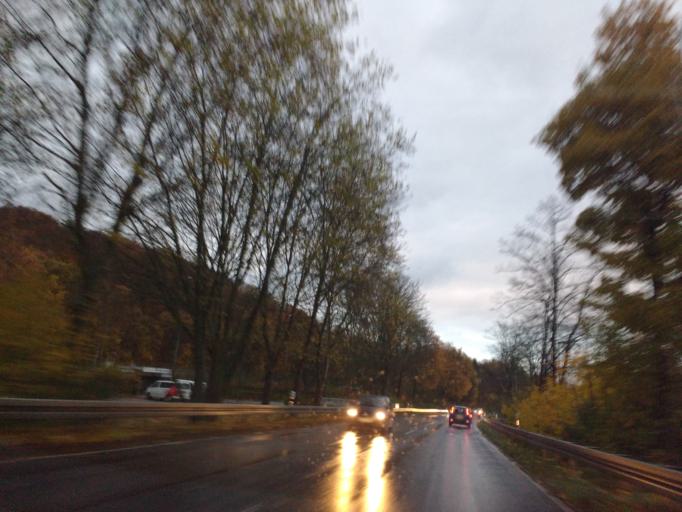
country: DE
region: Hesse
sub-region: Regierungsbezirk Kassel
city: Baunatal
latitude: 51.2592
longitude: 9.4041
